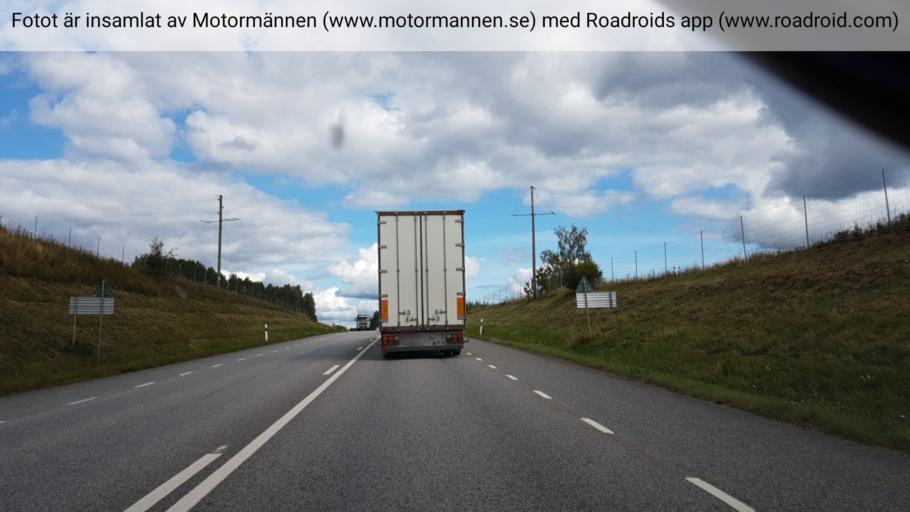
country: SE
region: Joenkoeping
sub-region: Tranas Kommun
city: Tranas
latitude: 58.0093
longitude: 14.9306
